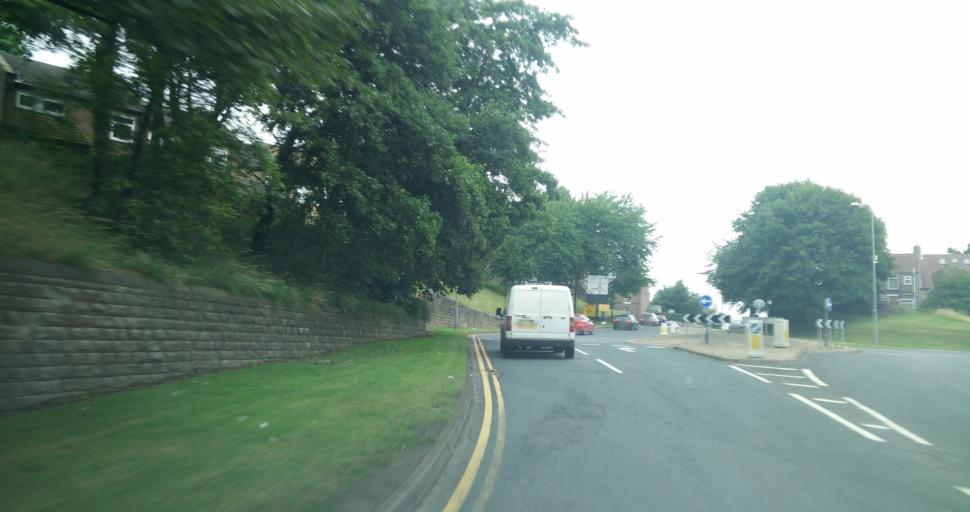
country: GB
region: England
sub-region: County Durham
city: Bishop Auckland
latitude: 54.6638
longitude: -1.6788
